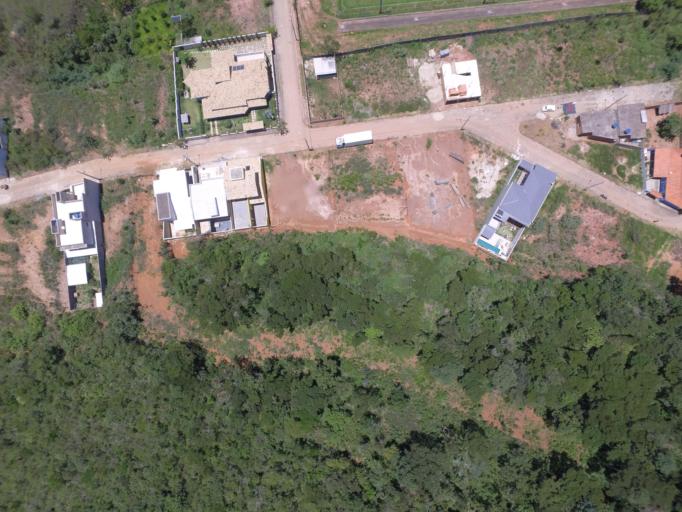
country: BR
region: Minas Gerais
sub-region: Tiradentes
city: Tiradentes
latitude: -21.0650
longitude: -44.0788
